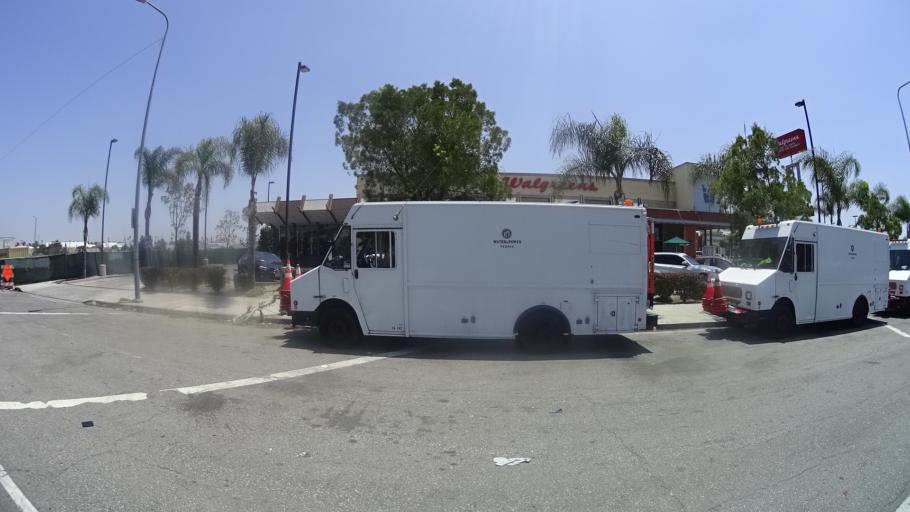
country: US
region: California
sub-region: Los Angeles County
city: View Park-Windsor Hills
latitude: 34.0192
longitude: -118.3351
